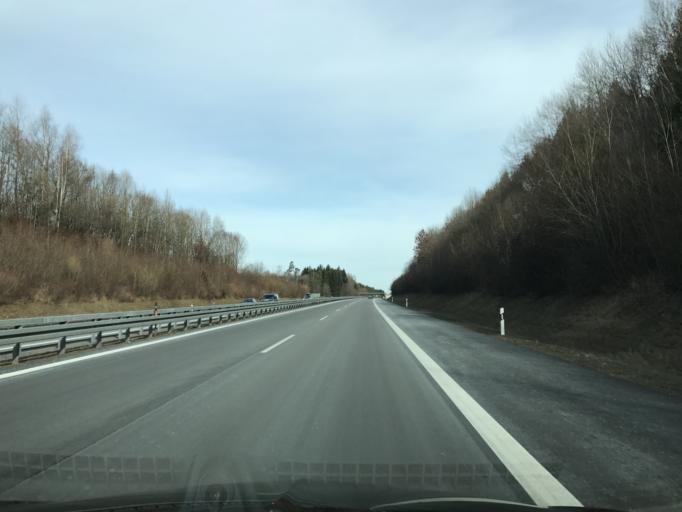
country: DE
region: Bavaria
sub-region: Swabia
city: Weissensberg
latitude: 47.6082
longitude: 9.7333
